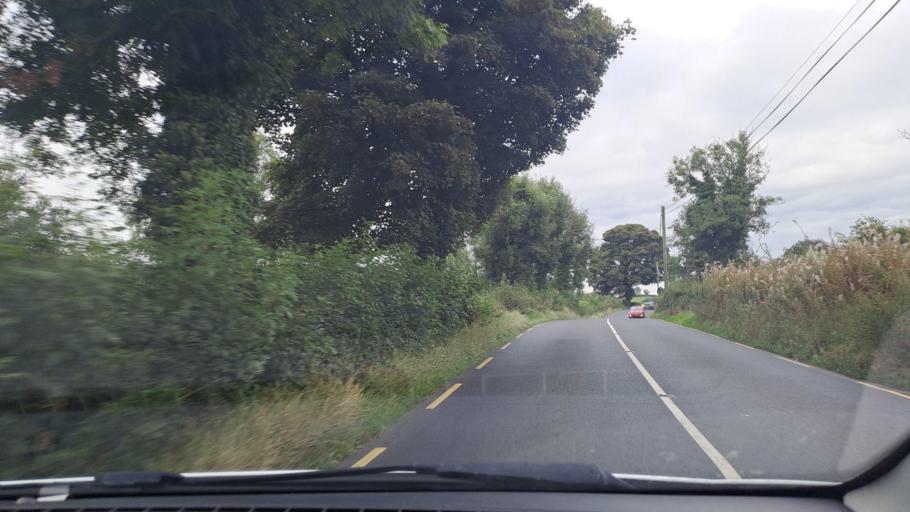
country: IE
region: Ulster
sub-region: An Cabhan
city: Kingscourt
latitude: 53.9964
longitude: -6.8502
